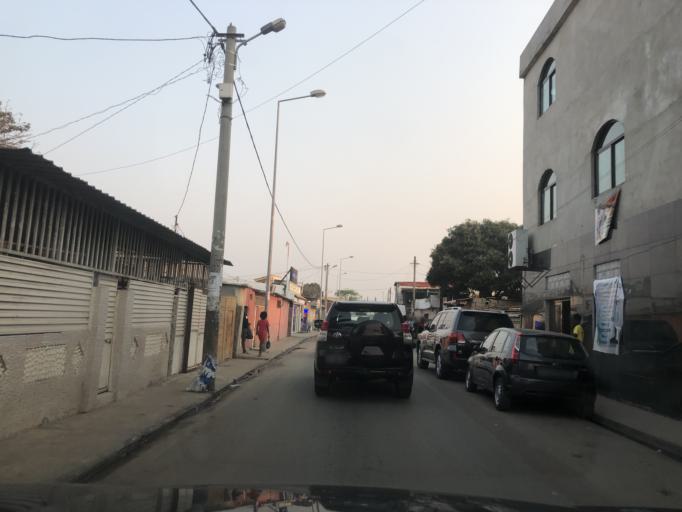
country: AO
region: Luanda
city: Luanda
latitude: -8.8443
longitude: 13.2248
